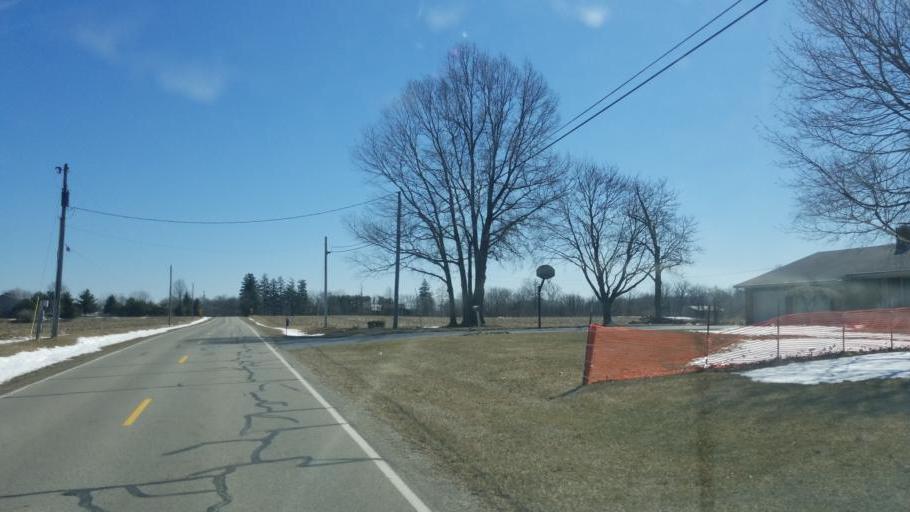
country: US
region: Ohio
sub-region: Crawford County
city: Bucyrus
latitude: 40.8046
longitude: -83.0132
